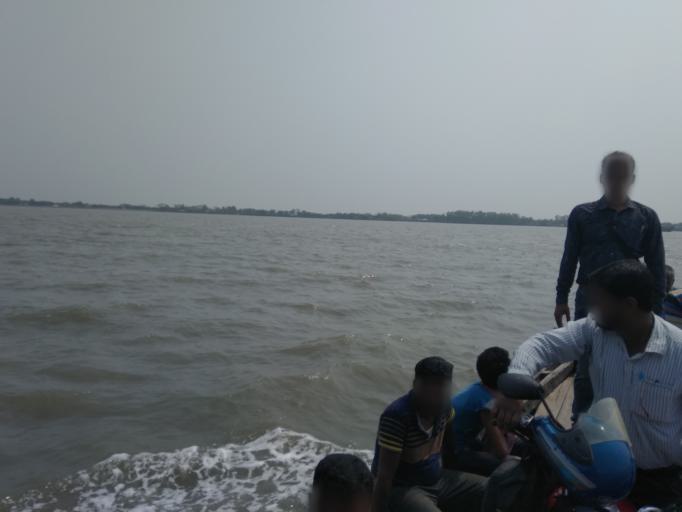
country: IN
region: West Bengal
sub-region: North 24 Parganas
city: Gosaba
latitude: 22.2496
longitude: 89.2437
